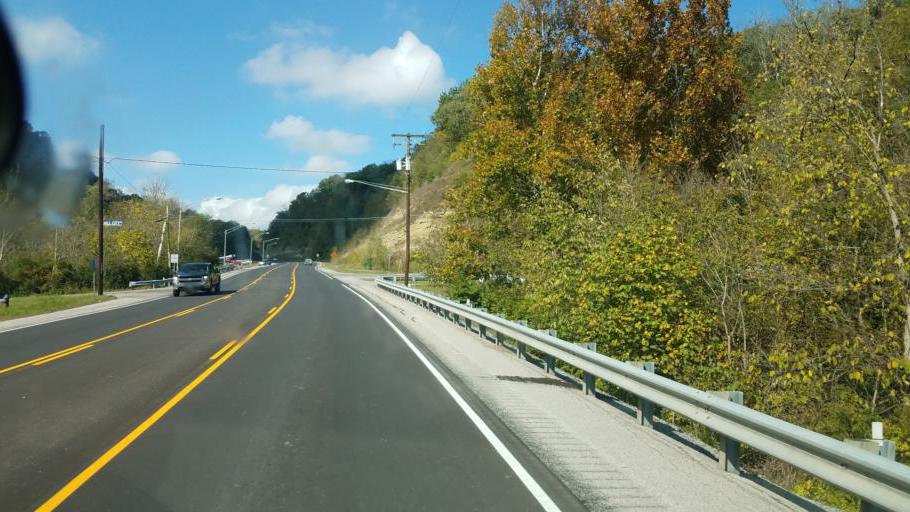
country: US
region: Ohio
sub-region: Brown County
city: Aberdeen
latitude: 38.6397
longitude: -83.7622
